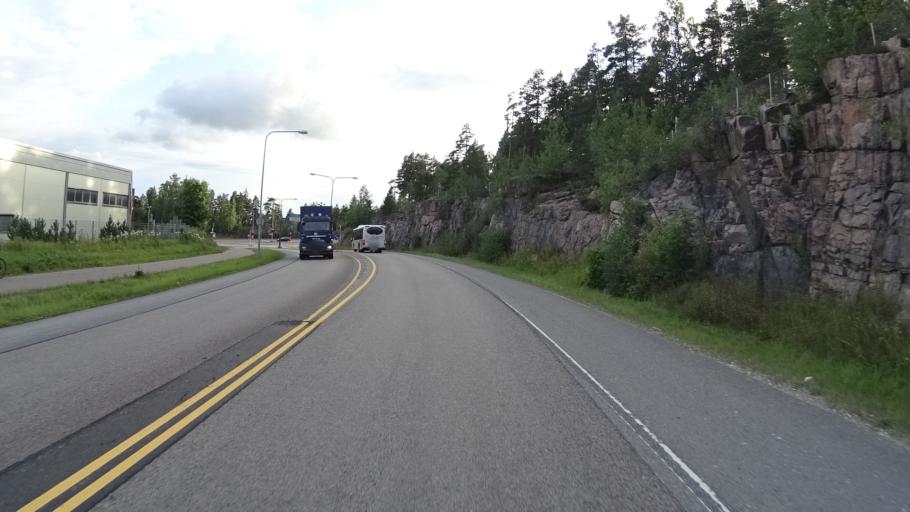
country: FI
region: Uusimaa
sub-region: Helsinki
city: Vantaa
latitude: 60.3036
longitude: 24.9846
